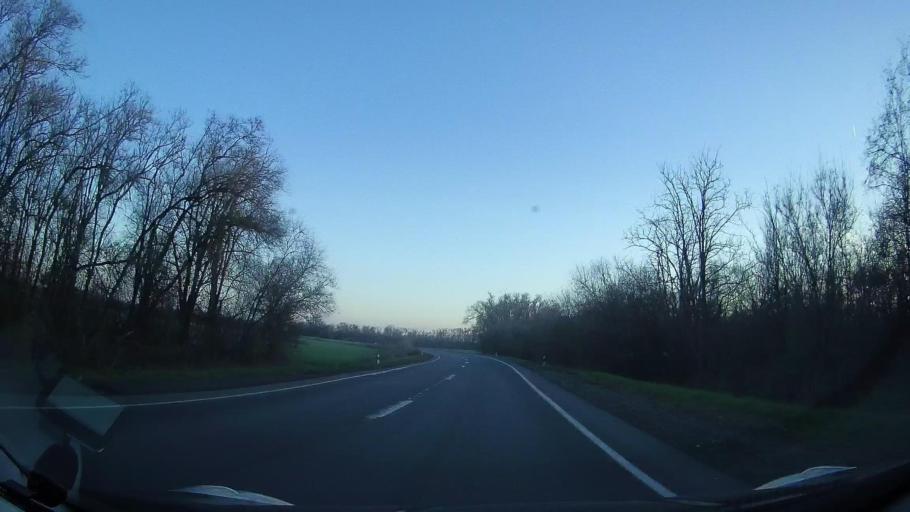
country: RU
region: Rostov
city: Bagayevskaya
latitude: 47.1006
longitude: 40.2768
